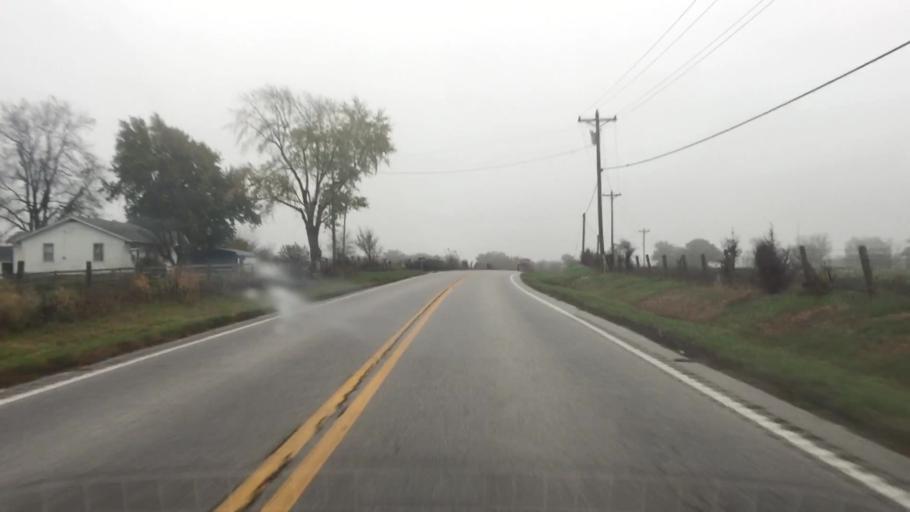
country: US
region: Missouri
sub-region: Callaway County
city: Fulton
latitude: 38.8634
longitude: -92.0080
